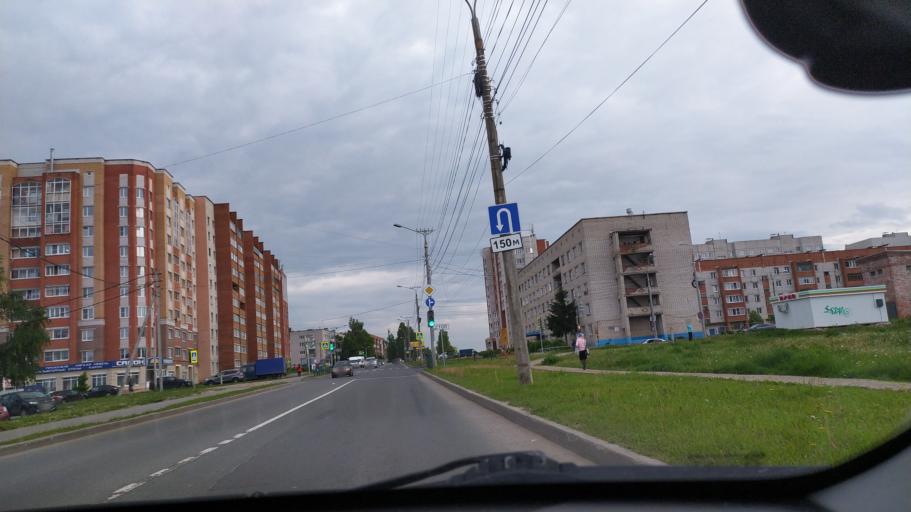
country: RU
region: Chuvashia
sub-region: Cheboksarskiy Rayon
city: Cheboksary
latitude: 56.1162
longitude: 47.2226
